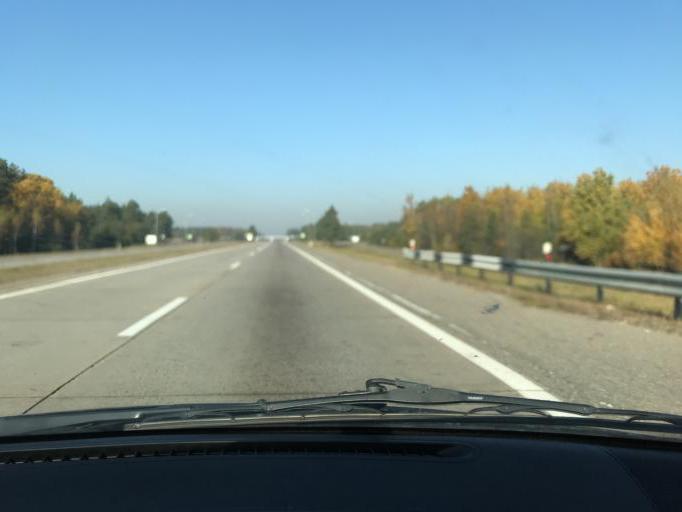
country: BY
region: Minsk
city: Slutsk
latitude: 53.3480
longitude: 27.5203
